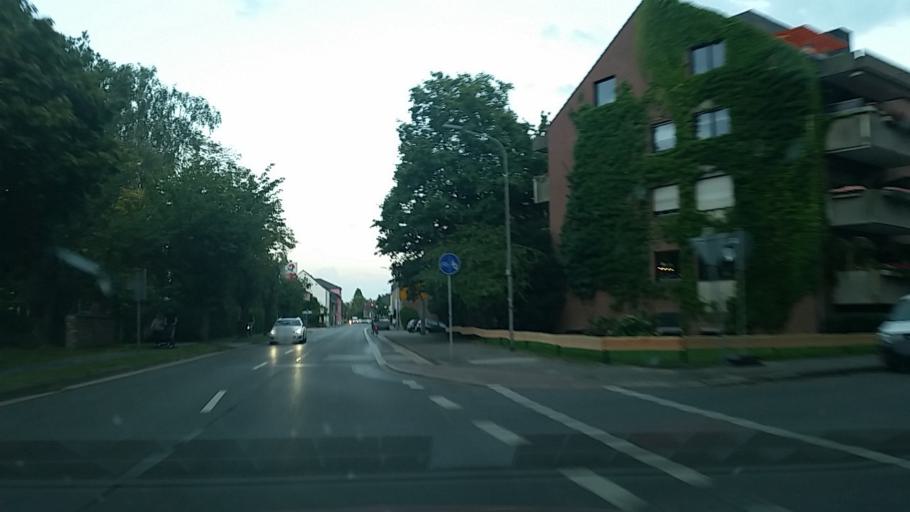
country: DE
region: North Rhine-Westphalia
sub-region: Regierungsbezirk Dusseldorf
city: Willich
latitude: 51.2666
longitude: 6.5499
